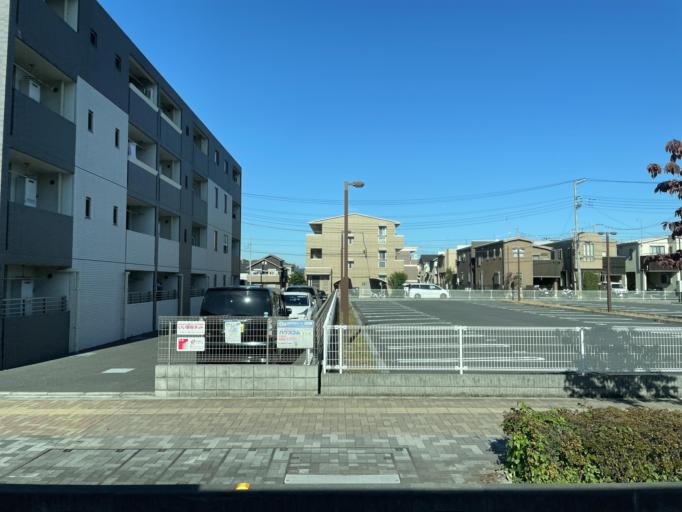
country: JP
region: Saitama
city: Asaka
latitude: 35.7999
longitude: 139.5665
